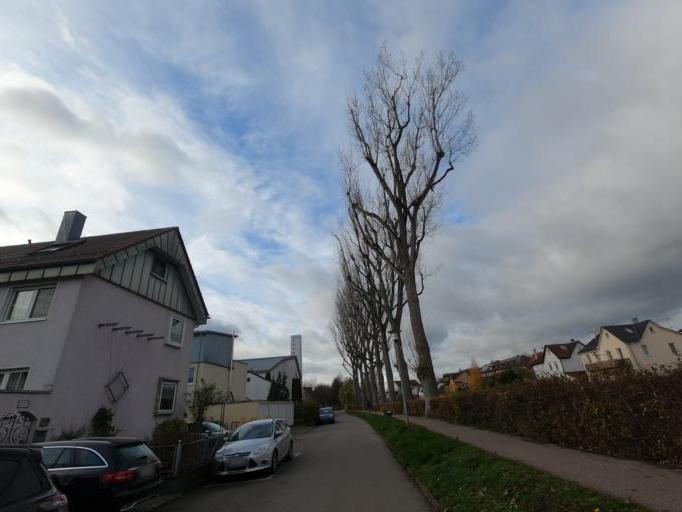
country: DE
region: Baden-Wuerttemberg
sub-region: Regierungsbezirk Stuttgart
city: Wangen
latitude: 48.7094
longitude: 9.6201
